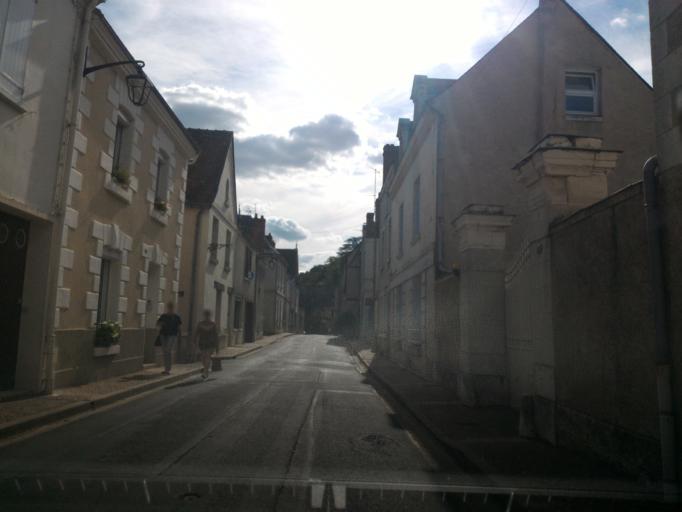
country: FR
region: Centre
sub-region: Departement d'Indre-et-Loire
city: Cangey
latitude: 47.4599
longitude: 1.0417
